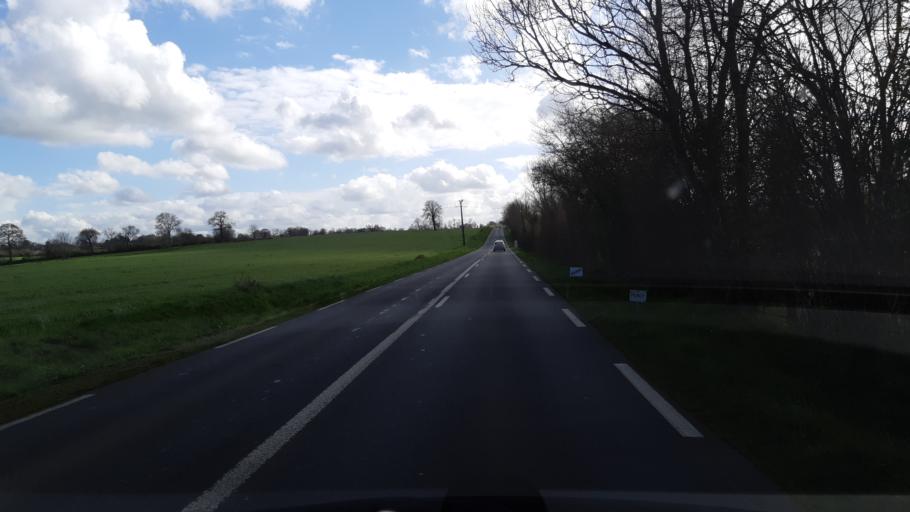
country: FR
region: Lower Normandy
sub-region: Departement de la Manche
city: Agneaux
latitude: 49.0443
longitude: -1.1286
